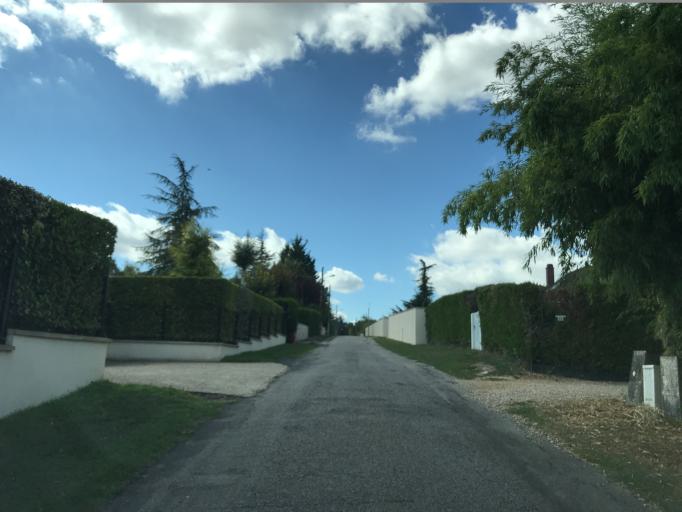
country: FR
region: Haute-Normandie
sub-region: Departement de l'Eure
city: Saint-Just
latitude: 49.1402
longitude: 1.4078
